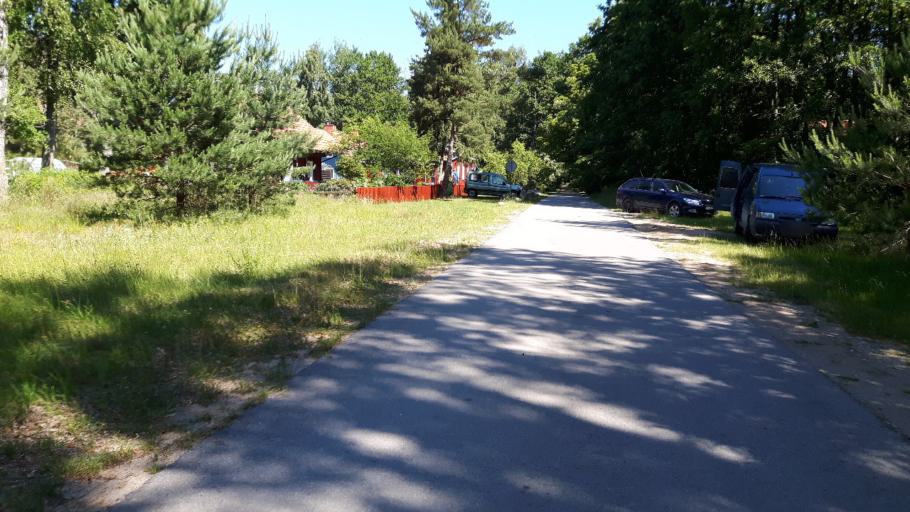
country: LT
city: Neringa
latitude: 55.3633
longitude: 21.0527
